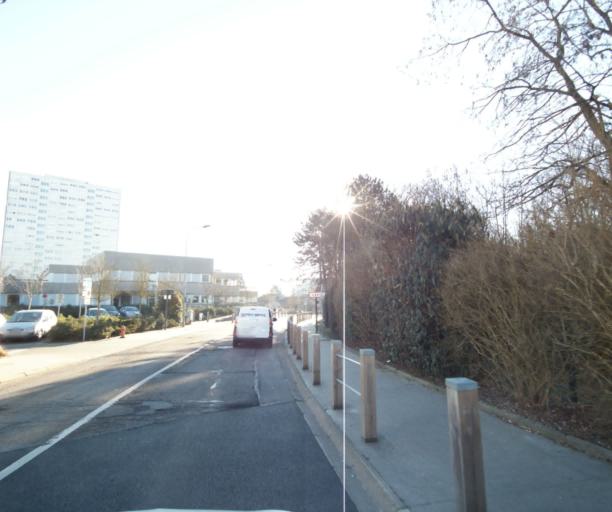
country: FR
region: Lorraine
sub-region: Departement de Meurthe-et-Moselle
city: Laxou
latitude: 48.6999
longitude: 6.1305
